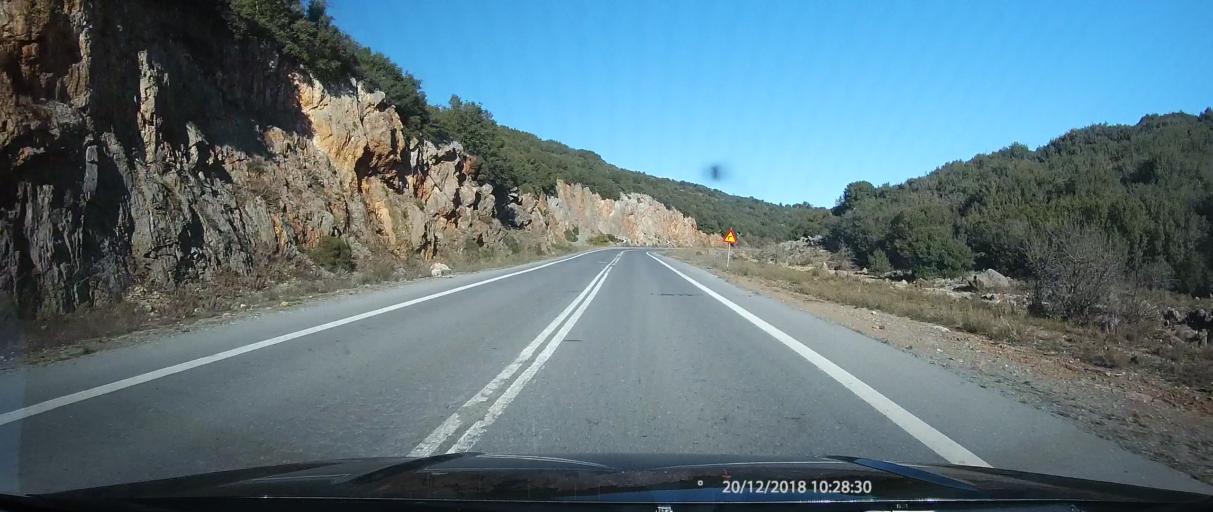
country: GR
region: Peloponnese
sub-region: Nomos Lakonias
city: Kariai
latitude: 37.2632
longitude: 22.4358
